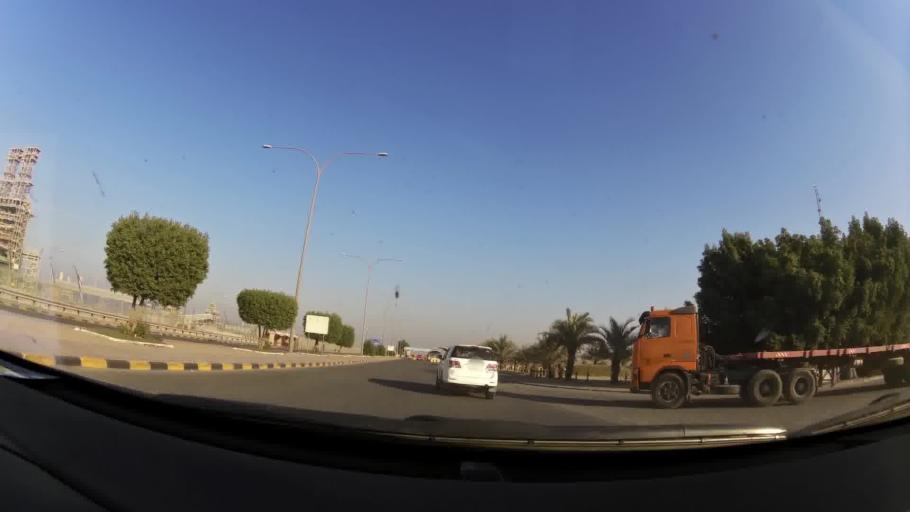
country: KW
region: Al Ahmadi
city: Al Fahahil
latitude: 29.0453
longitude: 48.1202
